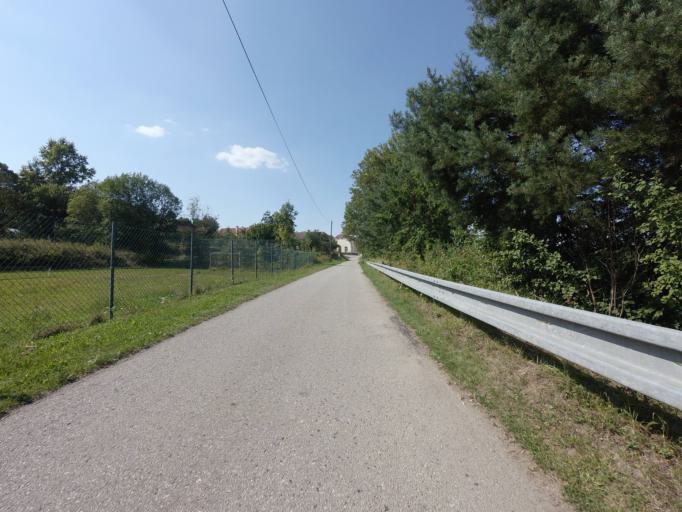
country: CZ
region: Jihocesky
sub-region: Okres Ceske Budejovice
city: Hluboka nad Vltavou
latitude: 49.1259
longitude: 14.4536
